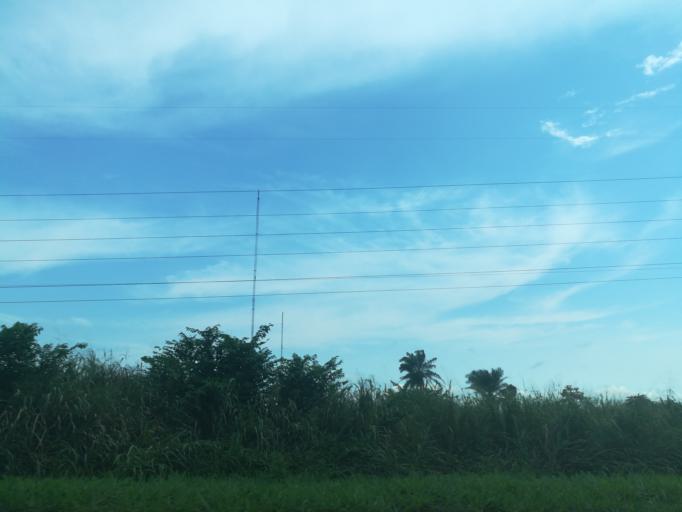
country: NG
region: Lagos
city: Ikorodu
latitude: 6.6355
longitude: 3.5268
